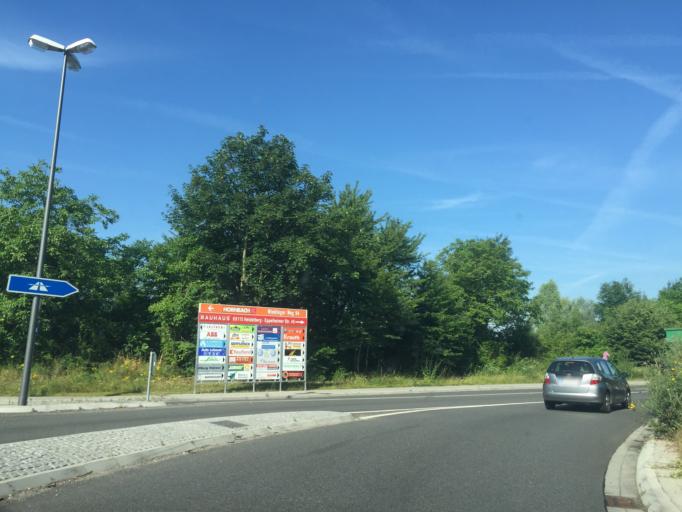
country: DE
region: Baden-Wuerttemberg
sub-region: Karlsruhe Region
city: Eppelheim
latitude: 49.4116
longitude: 8.6455
